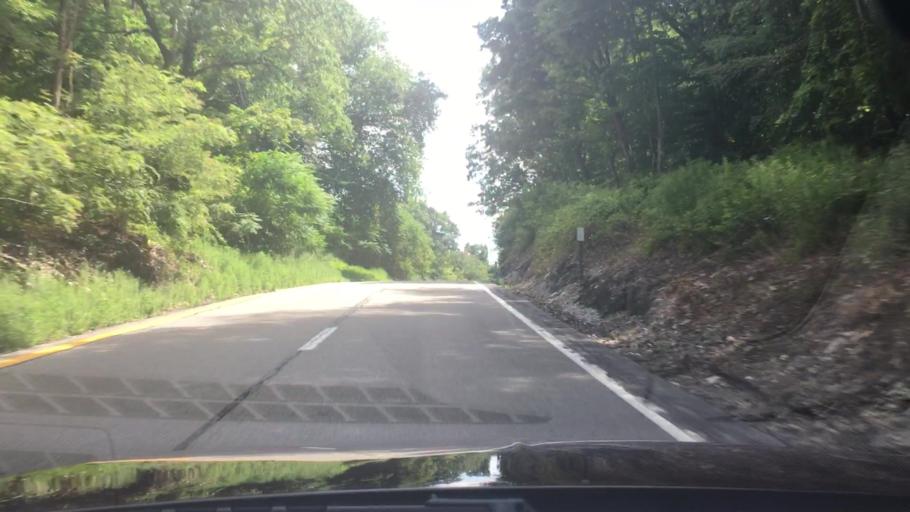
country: US
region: New York
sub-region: Dutchess County
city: Hillside Lake
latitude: 41.6213
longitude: -73.7679
